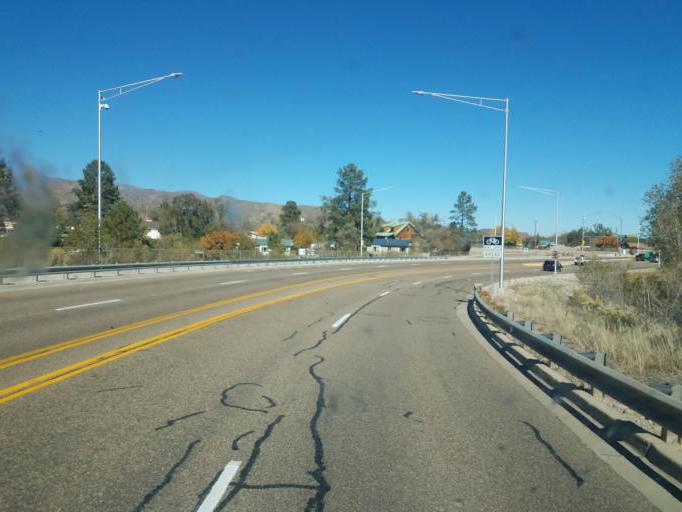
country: US
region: New Mexico
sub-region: Los Alamos County
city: Los Alamos
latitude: 35.8813
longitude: -106.3214
